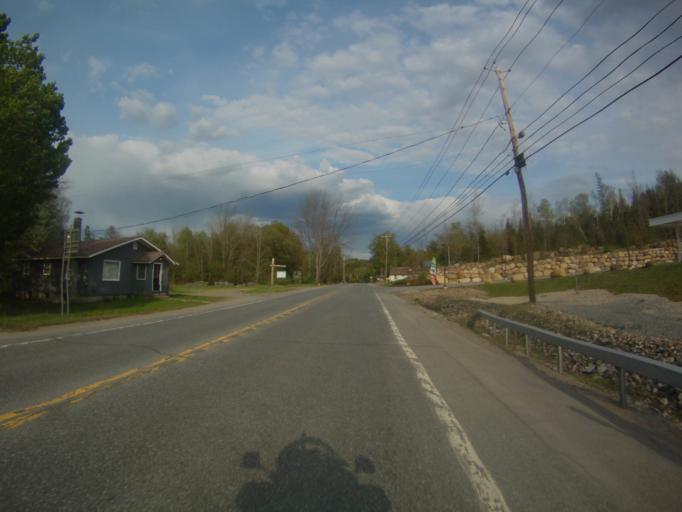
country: US
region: New York
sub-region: Warren County
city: Warrensburg
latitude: 43.6837
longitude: -73.9780
